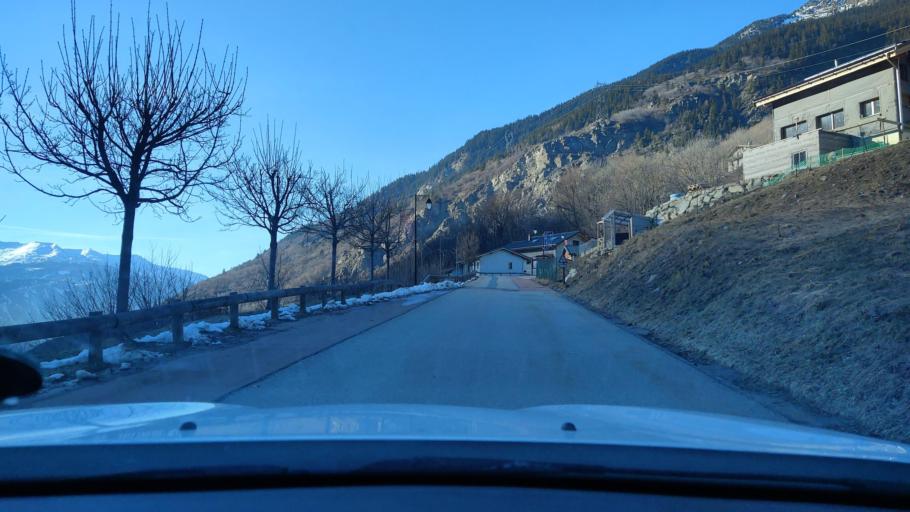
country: FR
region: Rhone-Alpes
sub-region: Departement de la Savoie
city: Saint-Michel-de-Maurienne
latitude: 45.2115
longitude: 6.5580
